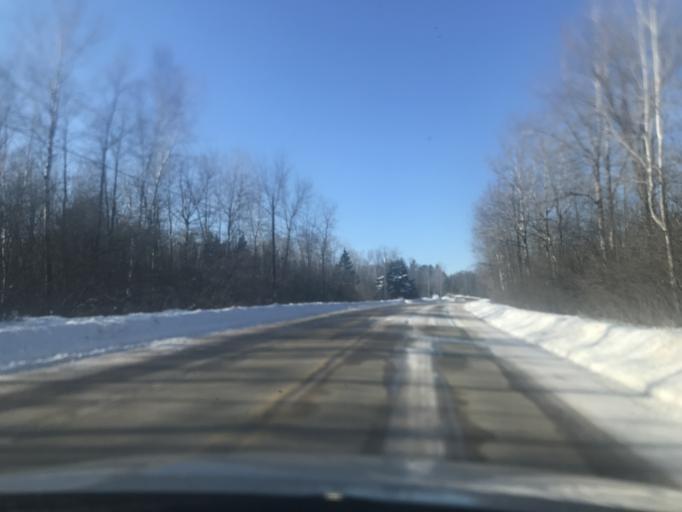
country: US
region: Wisconsin
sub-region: Marinette County
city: Marinette
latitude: 45.1494
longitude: -87.6866
